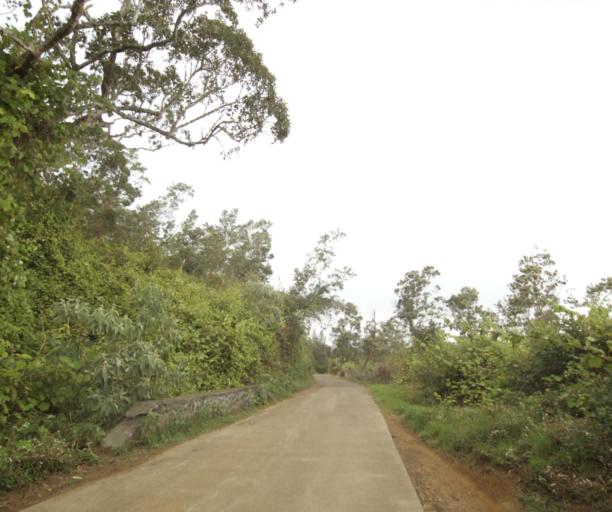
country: RE
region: Reunion
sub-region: Reunion
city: Saint-Paul
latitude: -21.0138
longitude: 55.3541
